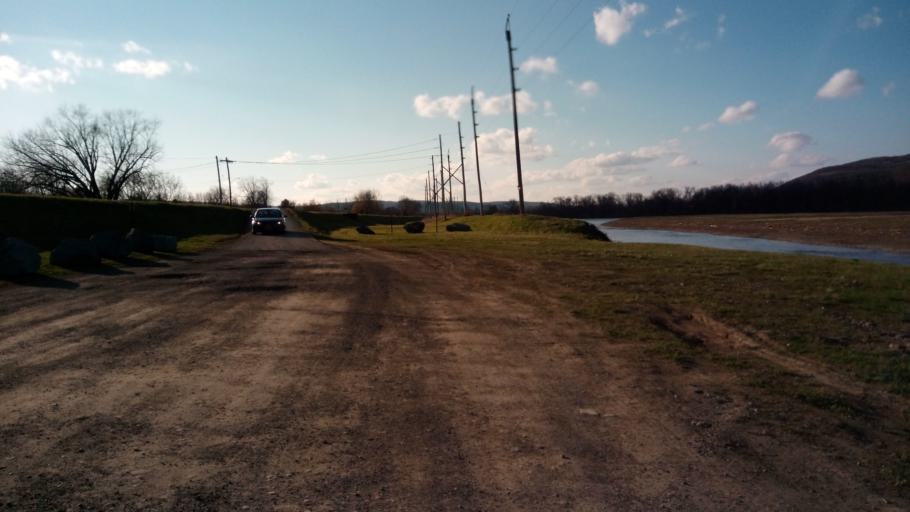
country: US
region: New York
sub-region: Chemung County
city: Elmira
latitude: 42.0814
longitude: -76.7803
